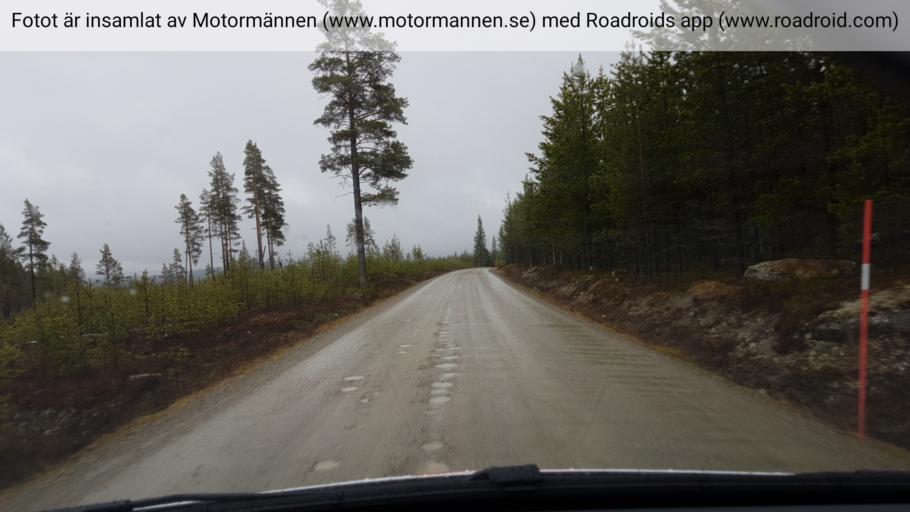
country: SE
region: Jaemtland
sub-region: Are Kommun
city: Jarpen
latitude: 62.4937
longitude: 13.5070
